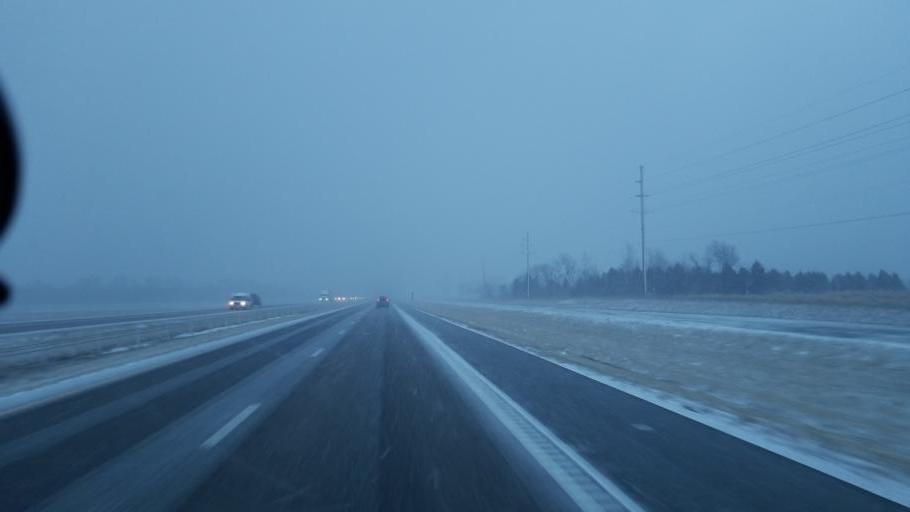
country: US
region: Missouri
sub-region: Montgomery County
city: Montgomery City
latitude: 38.8836
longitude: -91.4008
